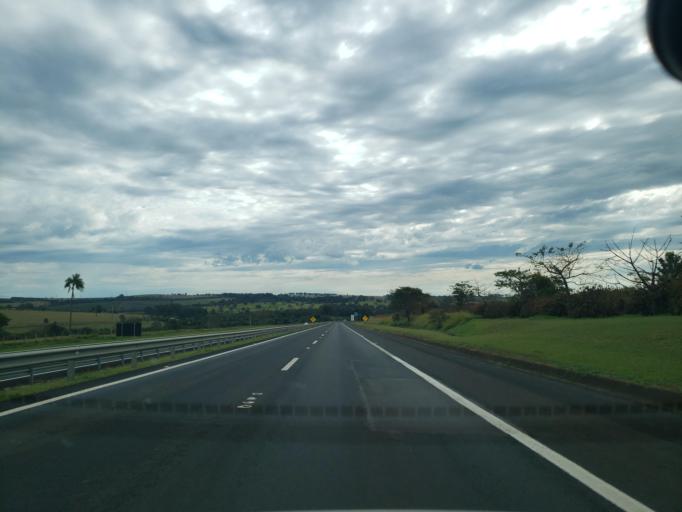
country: BR
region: Sao Paulo
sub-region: Bauru
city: Bauru
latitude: -22.2137
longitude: -49.1752
